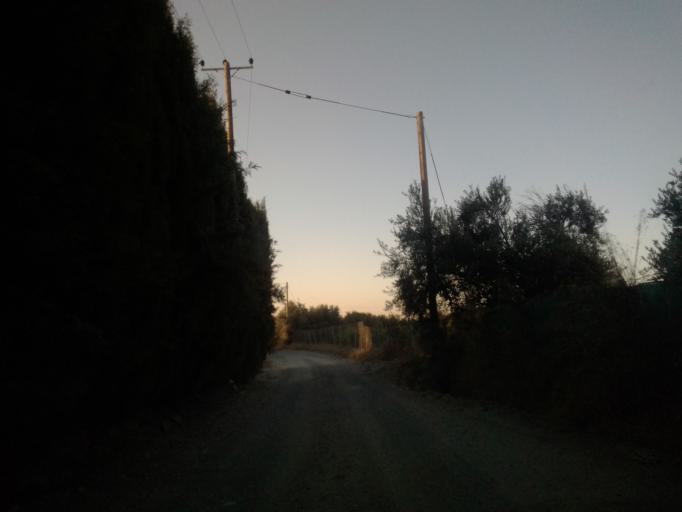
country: CY
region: Limassol
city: Ypsonas
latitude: 34.6708
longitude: 32.9650
